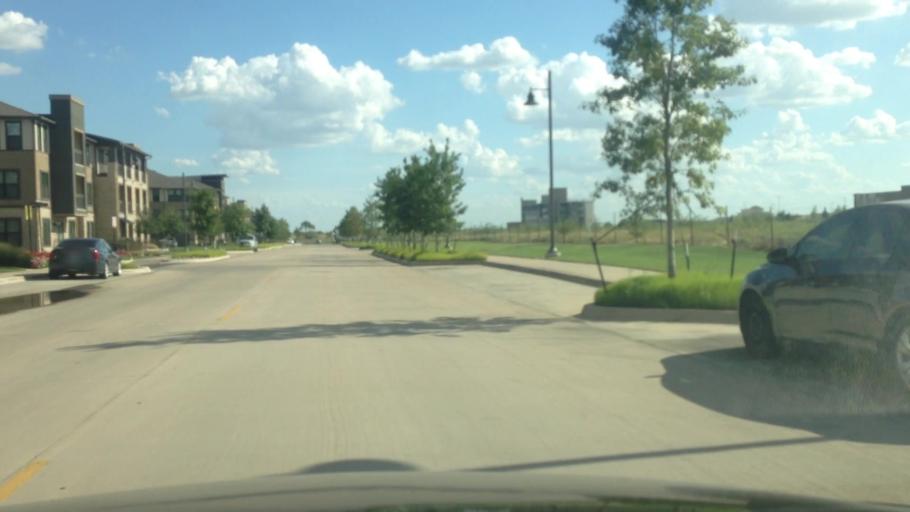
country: US
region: Texas
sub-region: Tarrant County
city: Blue Mound
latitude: 32.9088
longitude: -97.3114
